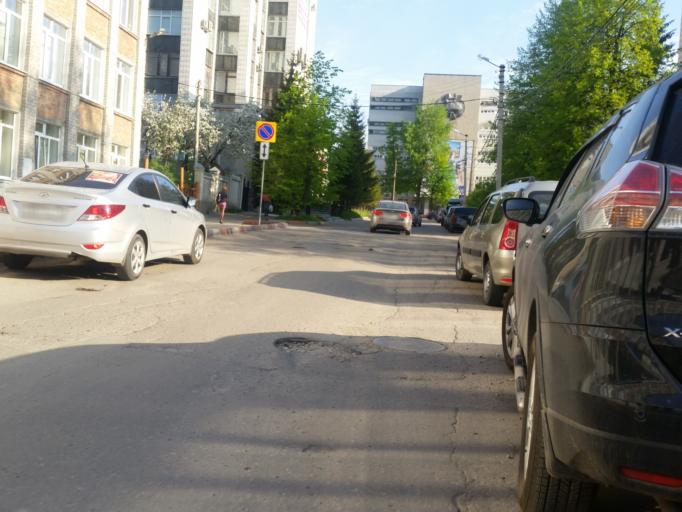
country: RU
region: Ulyanovsk
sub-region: Ulyanovskiy Rayon
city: Ulyanovsk
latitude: 54.3113
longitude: 48.3935
